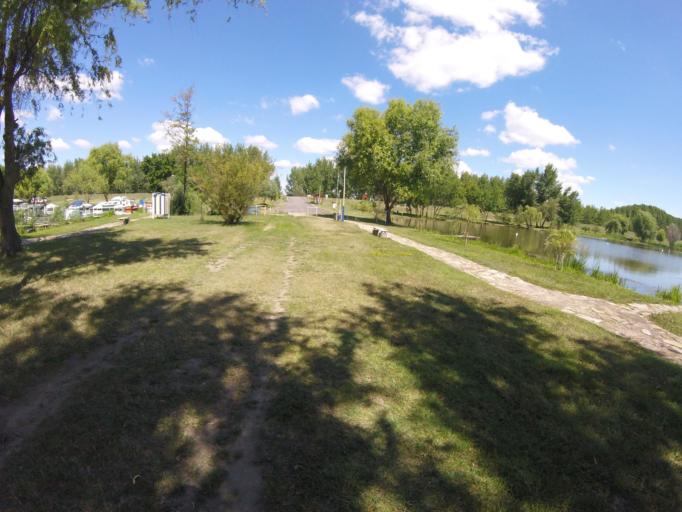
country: HU
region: Jasz-Nagykun-Szolnok
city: Abadszalok
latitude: 47.5156
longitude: 20.5756
